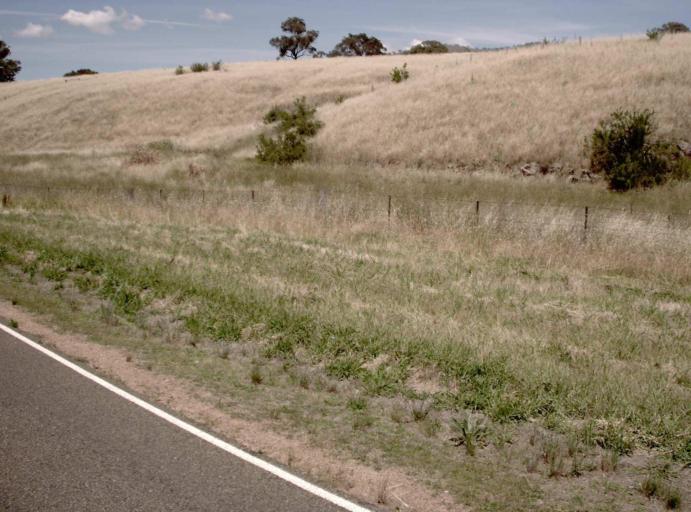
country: AU
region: Victoria
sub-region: East Gippsland
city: Bairnsdale
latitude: -37.2276
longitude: 147.7171
